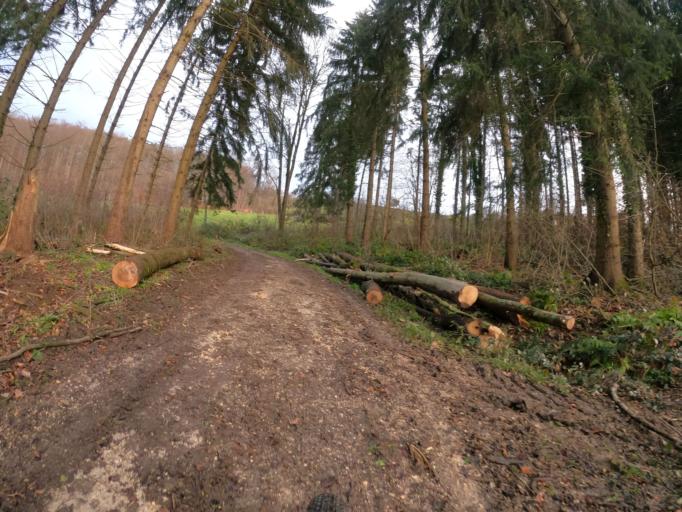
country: DE
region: Baden-Wuerttemberg
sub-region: Regierungsbezirk Stuttgart
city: Sussen
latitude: 48.6928
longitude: 9.7629
